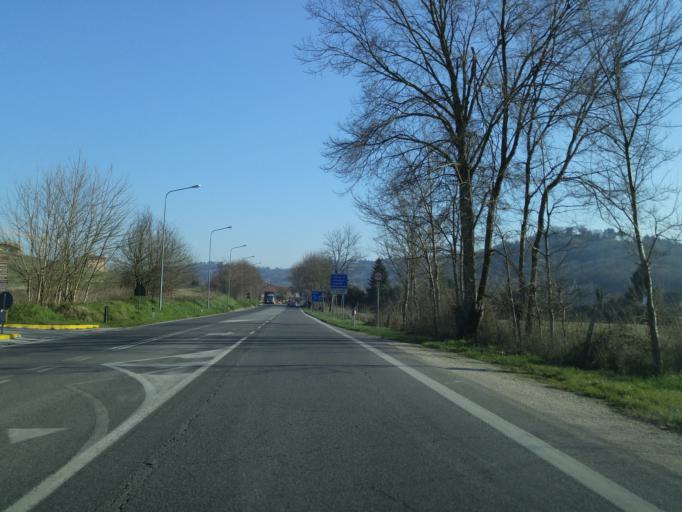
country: IT
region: The Marches
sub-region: Provincia di Pesaro e Urbino
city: Gradara
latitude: 43.9502
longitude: 12.7871
